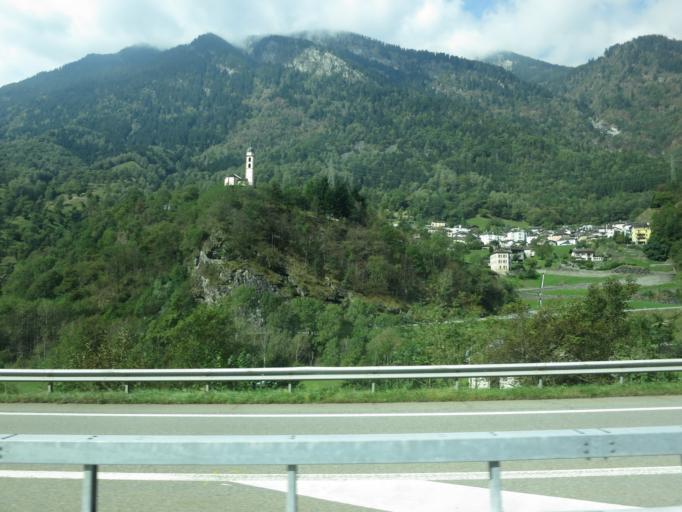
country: CH
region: Grisons
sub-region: Moesa District
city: Mesocco
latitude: 46.3639
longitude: 9.2270
